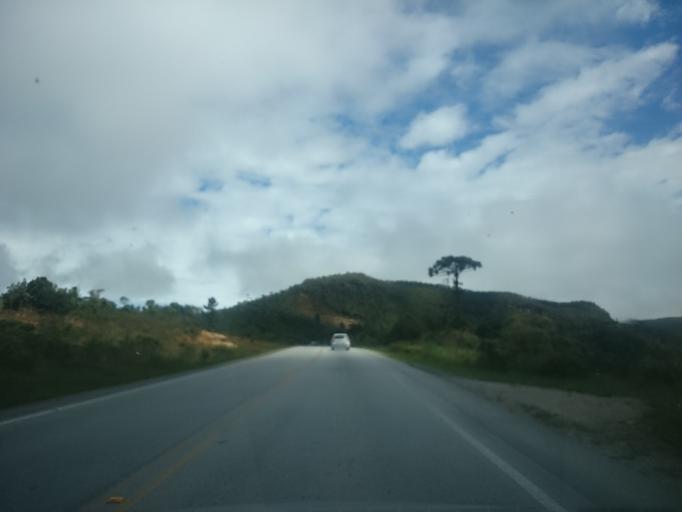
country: BR
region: Santa Catarina
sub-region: Anitapolis
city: Anitapolis
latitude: -27.6864
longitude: -49.1189
